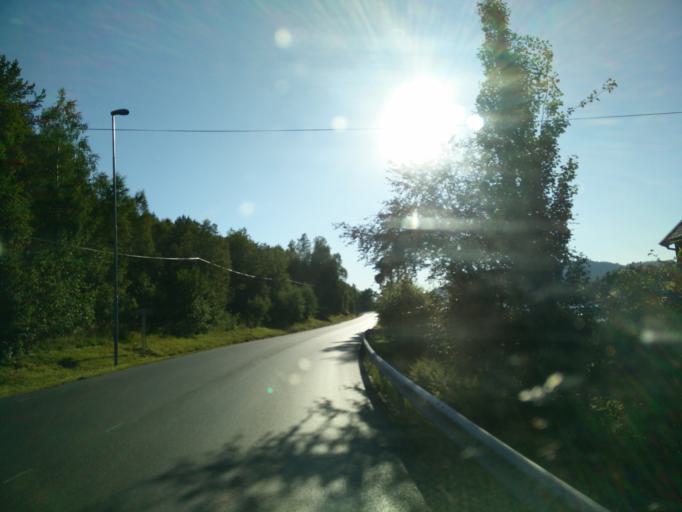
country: NO
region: More og Romsdal
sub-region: Halsa
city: Liaboen
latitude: 63.0841
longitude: 8.3474
